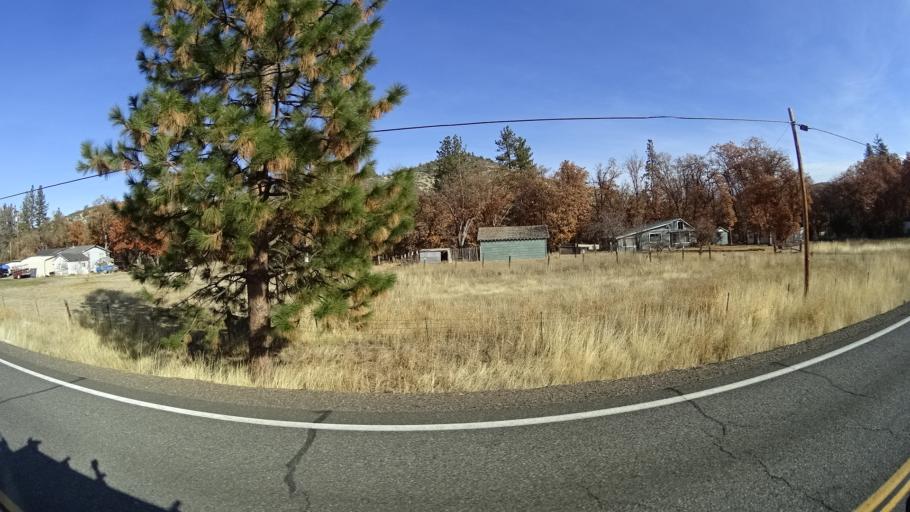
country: US
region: California
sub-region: Siskiyou County
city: Yreka
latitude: 41.6592
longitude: -122.5921
